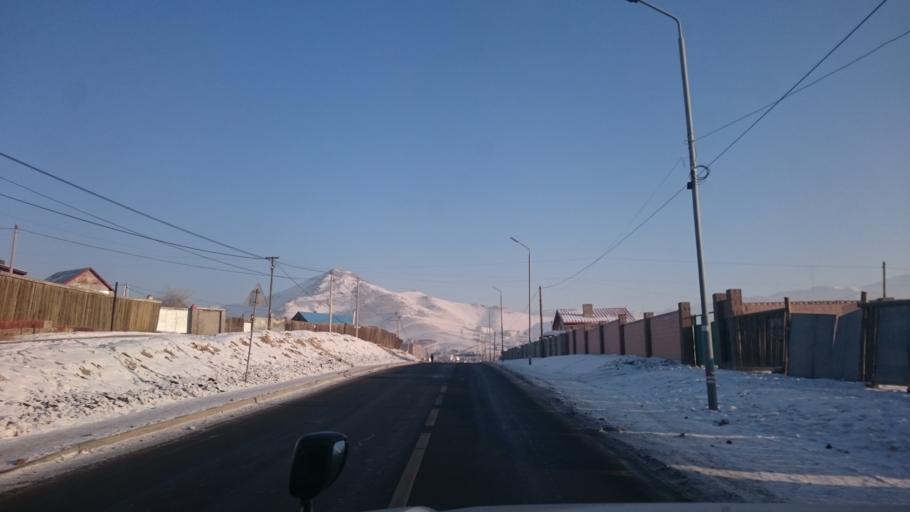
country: MN
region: Ulaanbaatar
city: Ulaanbaatar
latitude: 47.9258
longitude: 107.1419
